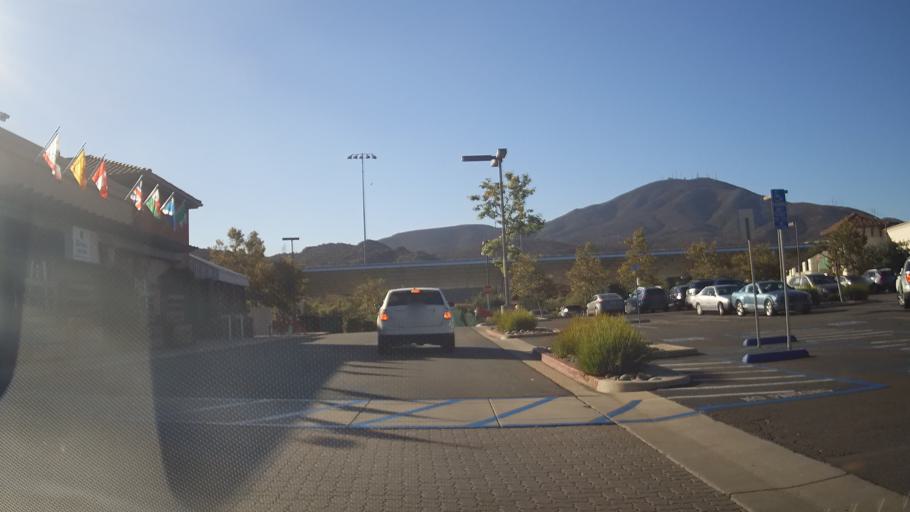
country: US
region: California
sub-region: San Diego County
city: Rancho San Diego
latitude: 32.7372
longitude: -116.9401
